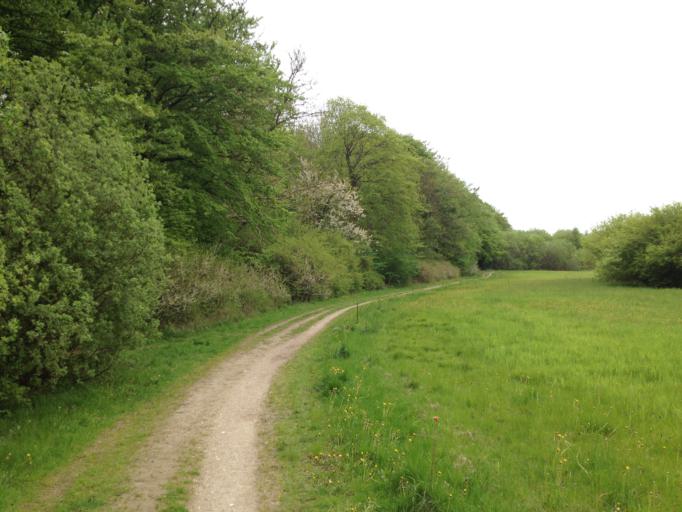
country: DK
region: Capital Region
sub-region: Fredensborg Kommune
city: Niva
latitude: 55.9476
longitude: 12.5171
